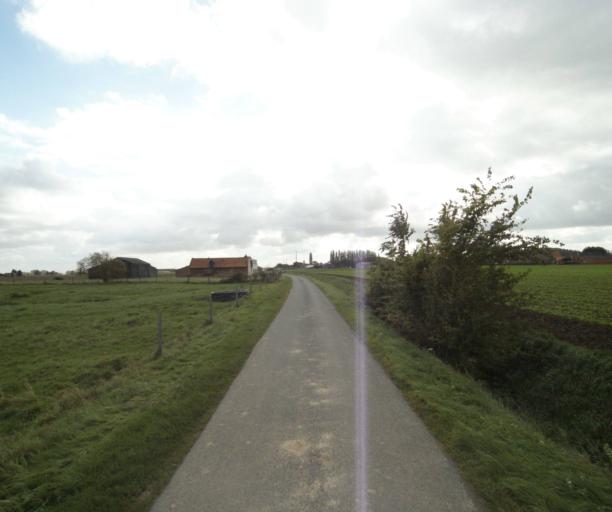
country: FR
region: Nord-Pas-de-Calais
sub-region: Departement du Nord
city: Frelinghien
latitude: 50.7108
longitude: 2.9539
